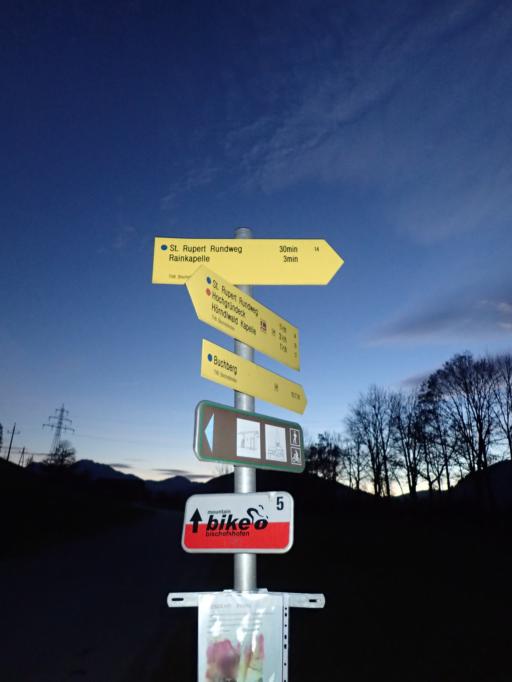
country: AT
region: Salzburg
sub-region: Politischer Bezirk Sankt Johann im Pongau
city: Bischofshofen
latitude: 47.4192
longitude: 13.2317
